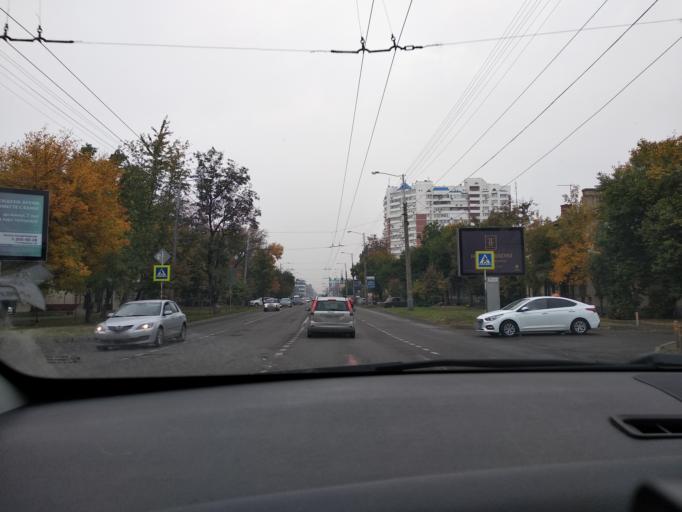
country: RU
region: Krasnodarskiy
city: Krasnodar
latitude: 45.0547
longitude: 38.9602
